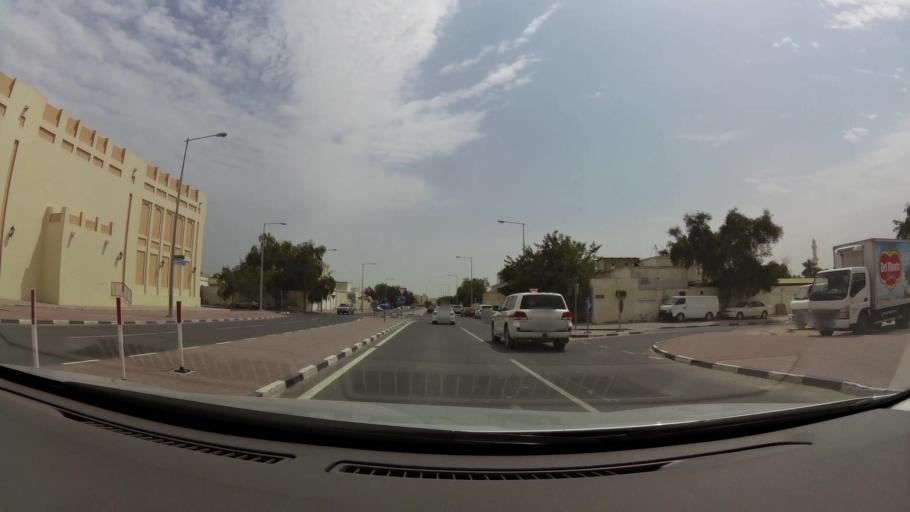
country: QA
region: Baladiyat ar Rayyan
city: Ar Rayyan
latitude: 25.3260
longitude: 51.4722
